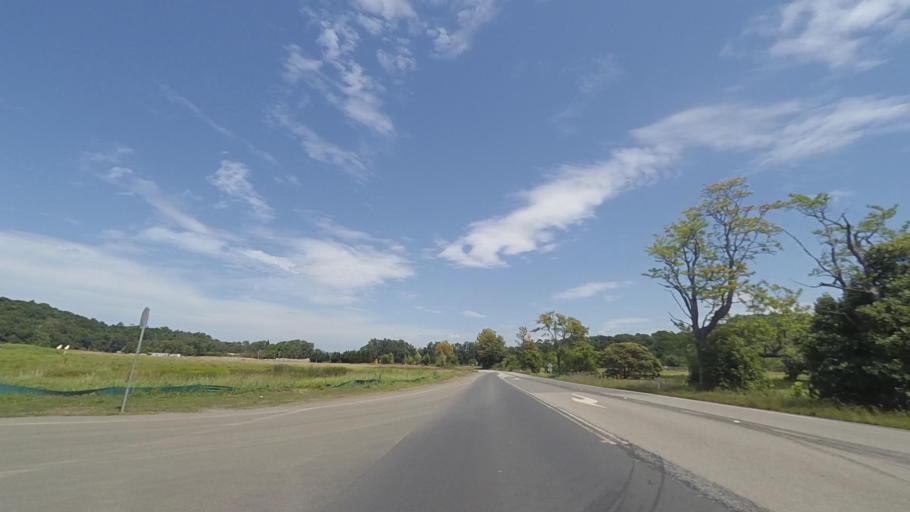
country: AU
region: New South Wales
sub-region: Kiama
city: Gerringong
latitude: -34.7422
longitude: 150.7616
